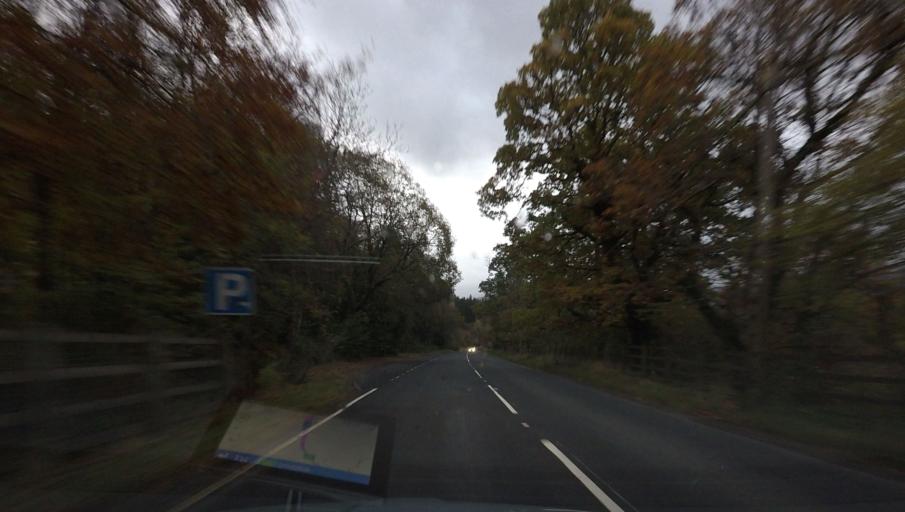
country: GB
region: Scotland
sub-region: Stirling
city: Callander
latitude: 56.3371
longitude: -4.3249
